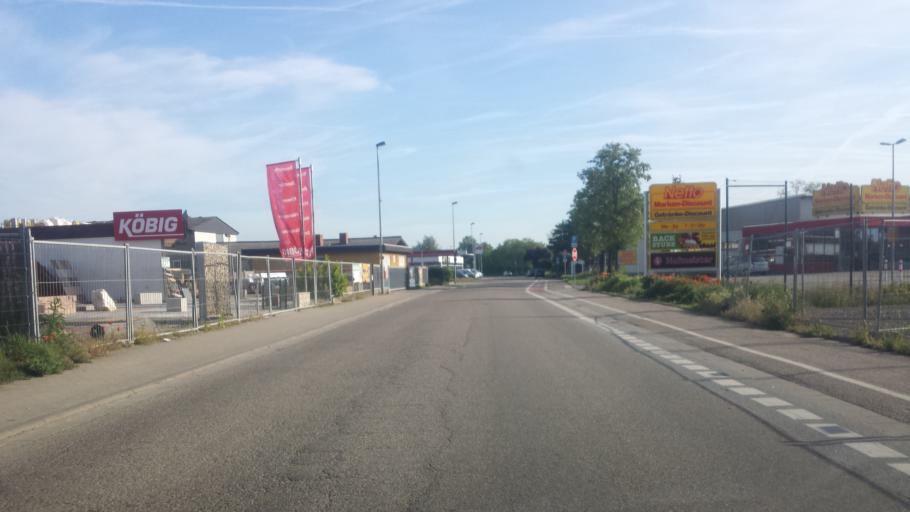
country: DE
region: Hesse
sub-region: Regierungsbezirk Darmstadt
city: Burstadt
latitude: 49.6460
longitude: 8.4698
